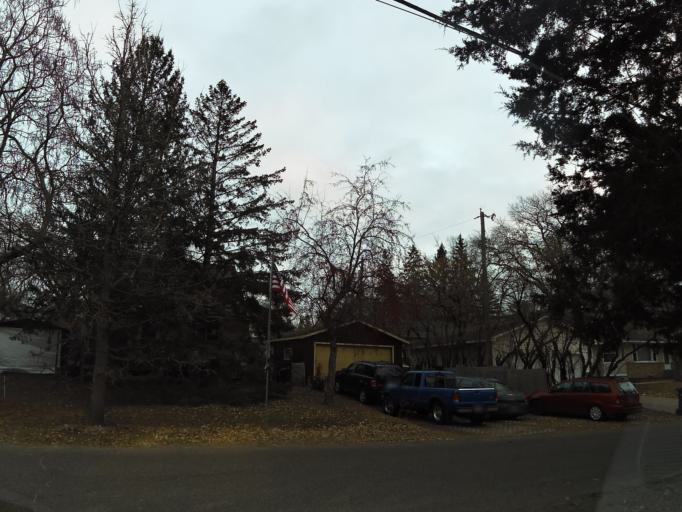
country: US
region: Minnesota
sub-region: Washington County
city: Mahtomedi
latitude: 45.0560
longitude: -92.9597
